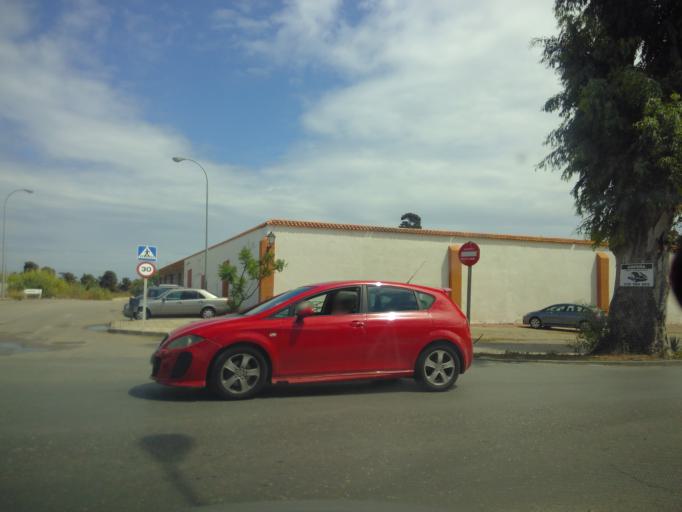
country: ES
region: Andalusia
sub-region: Provincia de Cadiz
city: La Linea de la Concepcion
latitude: 36.1837
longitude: -5.3496
